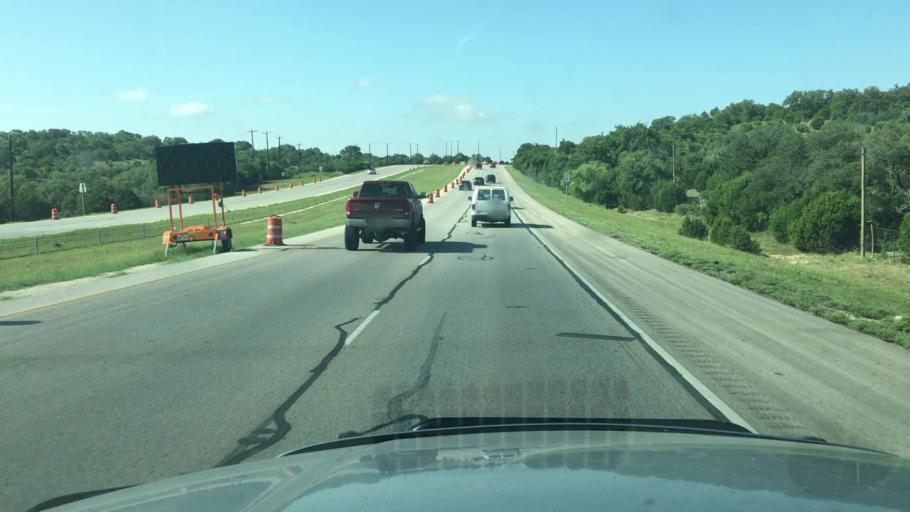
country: US
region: Texas
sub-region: Comal County
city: Bulverde
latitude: 29.7695
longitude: -98.4313
